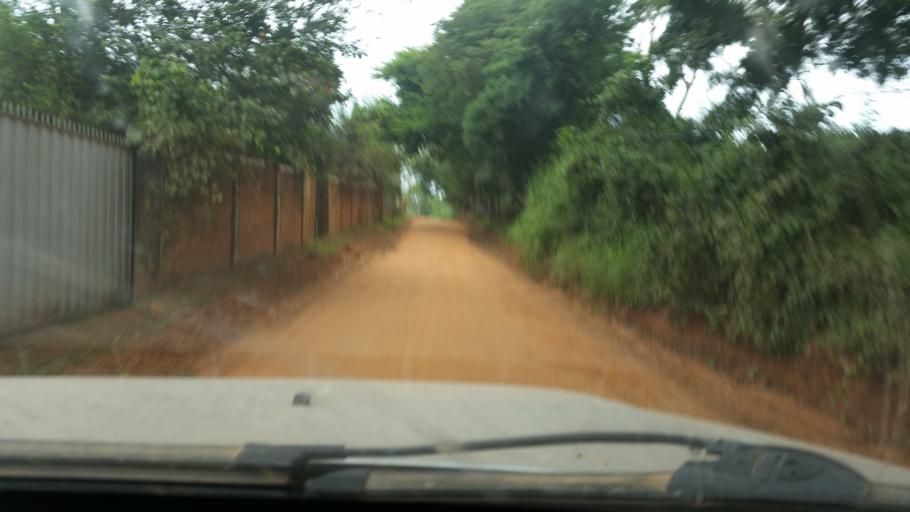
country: PY
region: Guaira
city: Independencia
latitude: -25.7035
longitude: -56.1917
